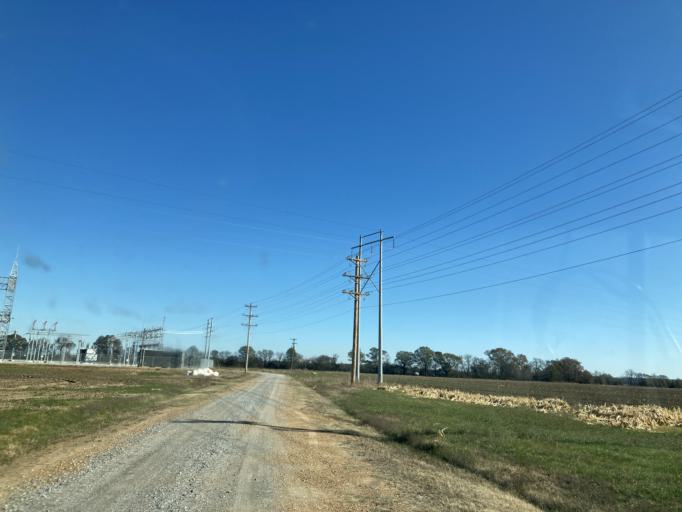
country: US
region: Mississippi
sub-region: Yazoo County
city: Yazoo City
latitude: 32.9157
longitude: -90.4472
